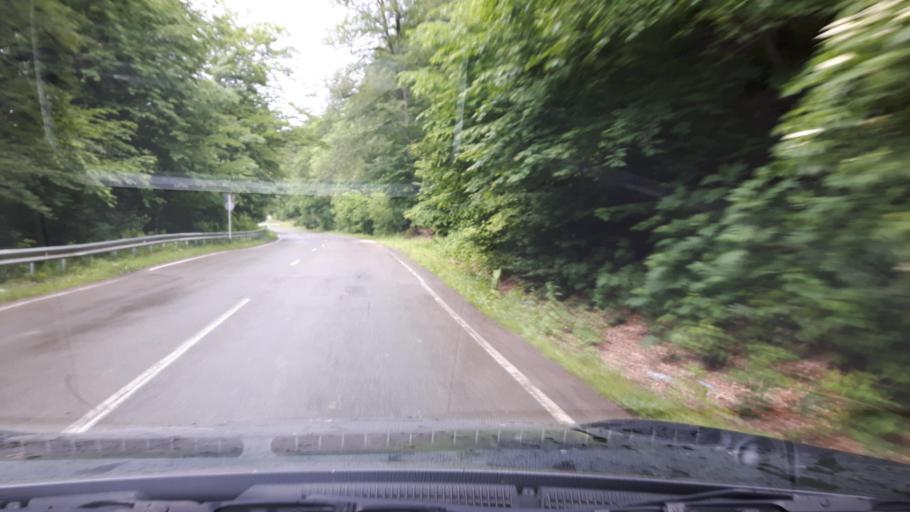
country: GE
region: Kakheti
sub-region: Telavi
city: Telavi
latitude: 41.8797
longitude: 45.3572
